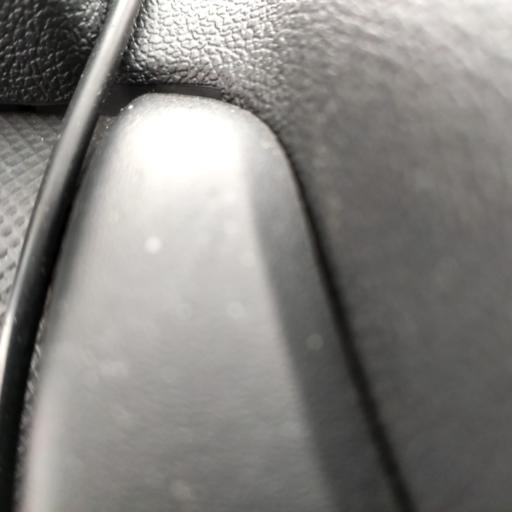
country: RU
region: Voronezj
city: Ostrogozhsk
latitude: 50.8415
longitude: 39.0296
